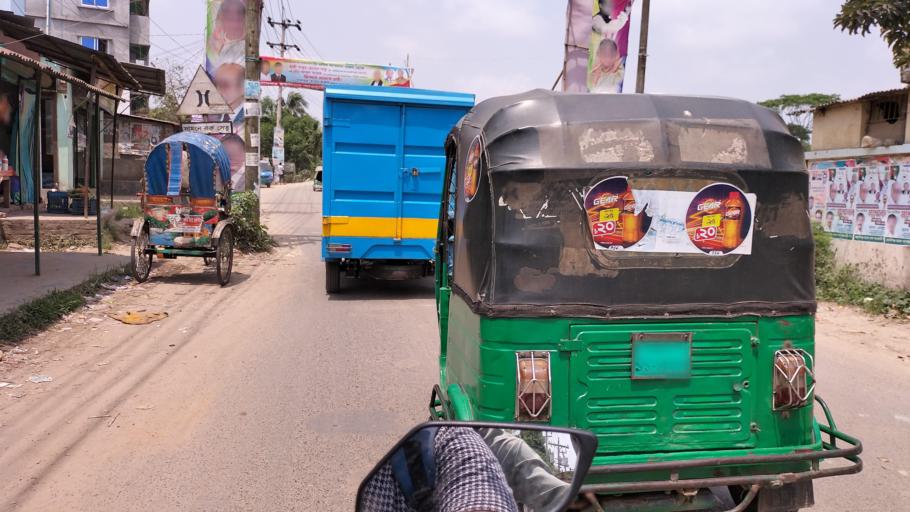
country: BD
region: Dhaka
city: Azimpur
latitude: 23.7313
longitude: 90.3147
